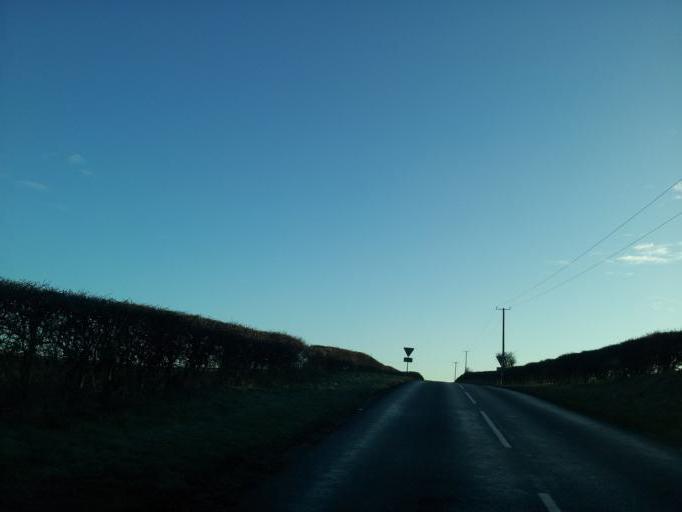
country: GB
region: England
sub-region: Lincolnshire
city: Horncastle
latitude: 53.2598
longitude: -0.0895
